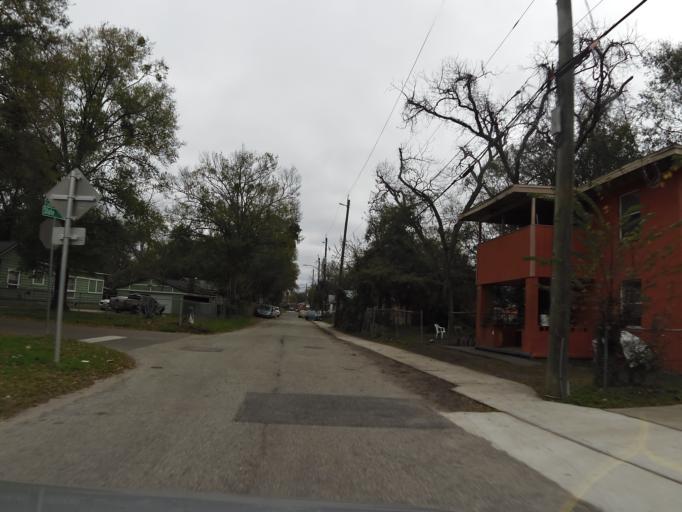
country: US
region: Florida
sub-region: Duval County
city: Jacksonville
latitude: 30.3383
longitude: -81.6840
